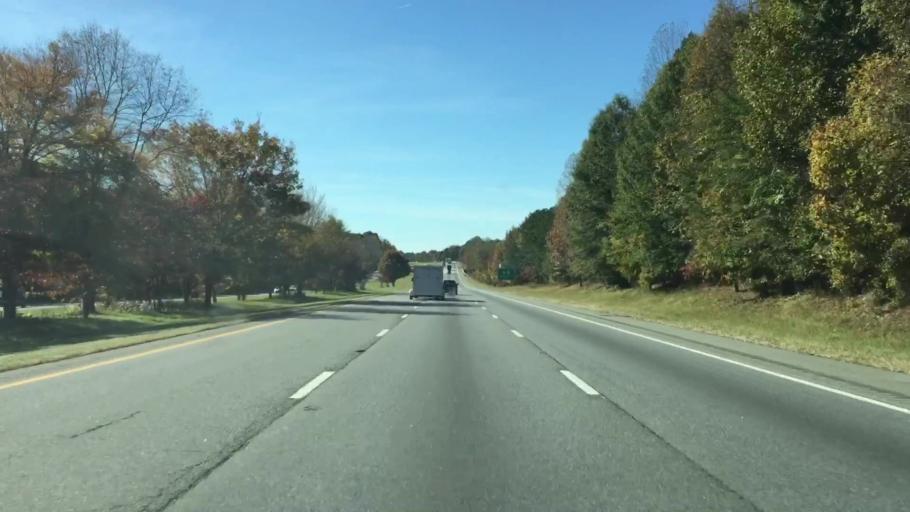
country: US
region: North Carolina
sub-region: Davidson County
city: Lexington
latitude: 35.7769
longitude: -80.2886
